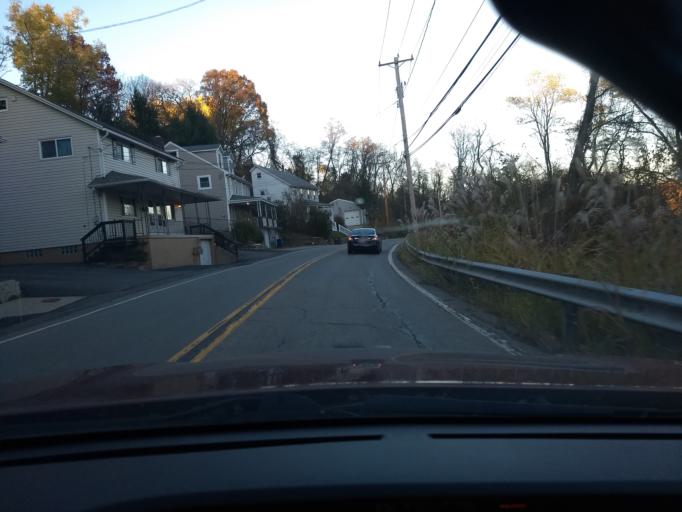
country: US
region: Pennsylvania
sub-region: Allegheny County
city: Pleasant Hills
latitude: 40.3509
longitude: -79.9674
